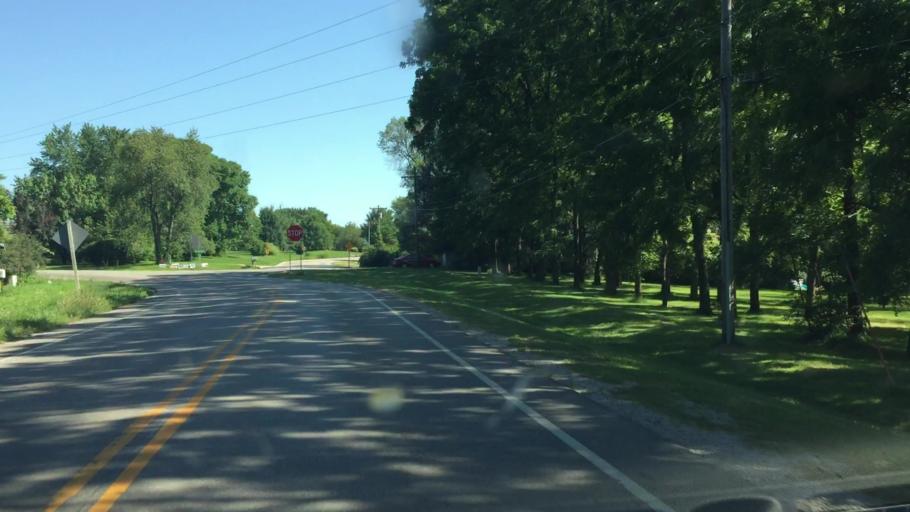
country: US
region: Iowa
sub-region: Linn County
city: Ely
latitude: 41.8352
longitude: -91.6361
